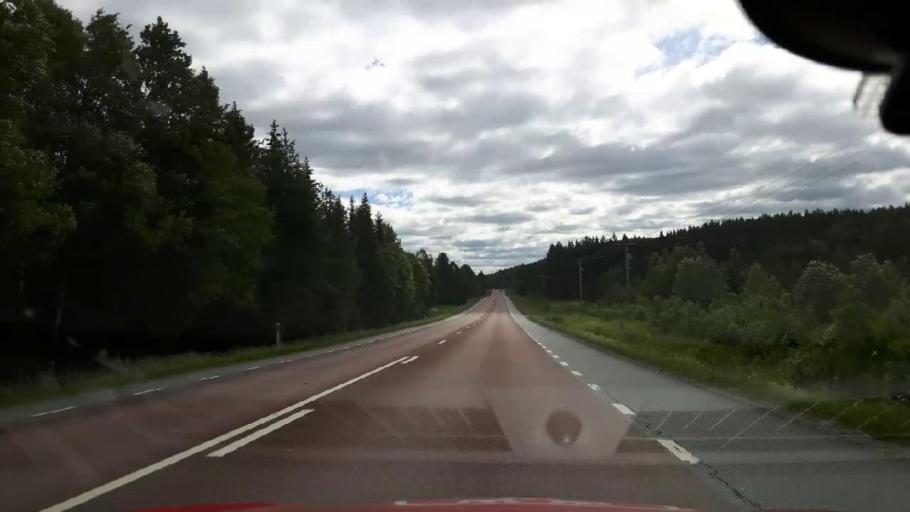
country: SE
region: Jaemtland
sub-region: Braecke Kommun
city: Braecke
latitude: 62.9439
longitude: 15.1764
